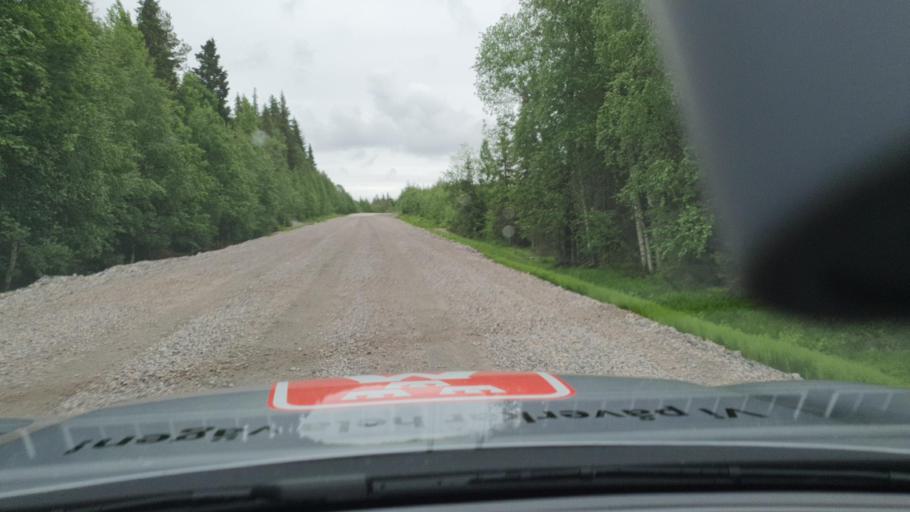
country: SE
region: Norrbotten
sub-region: Overtornea Kommun
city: OEvertornea
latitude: 66.5458
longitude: 23.3502
